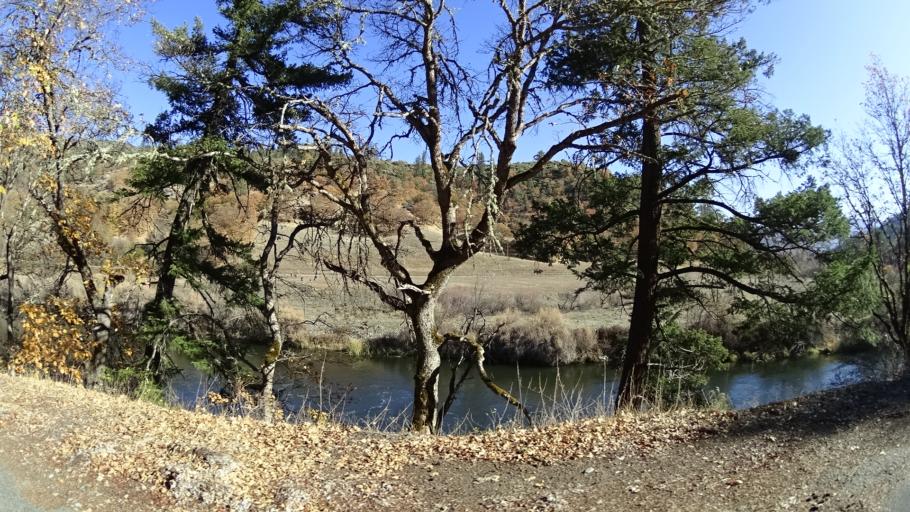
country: US
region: California
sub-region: Siskiyou County
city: Yreka
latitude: 41.8446
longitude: -122.9007
